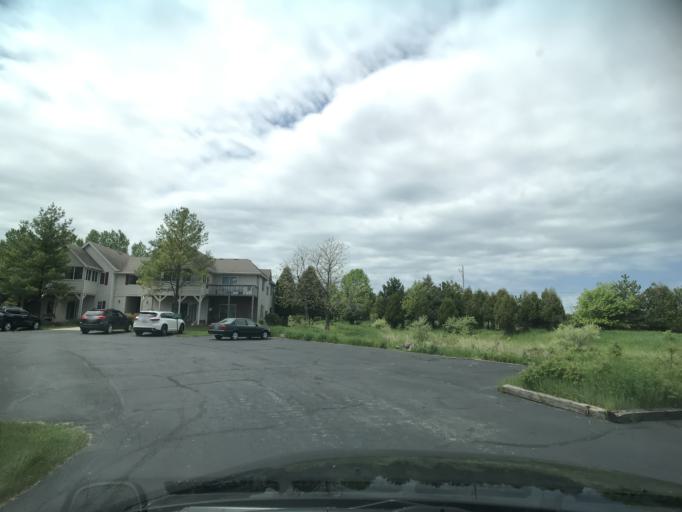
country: US
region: Wisconsin
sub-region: Door County
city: Sturgeon Bay
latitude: 45.1785
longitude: -87.1510
